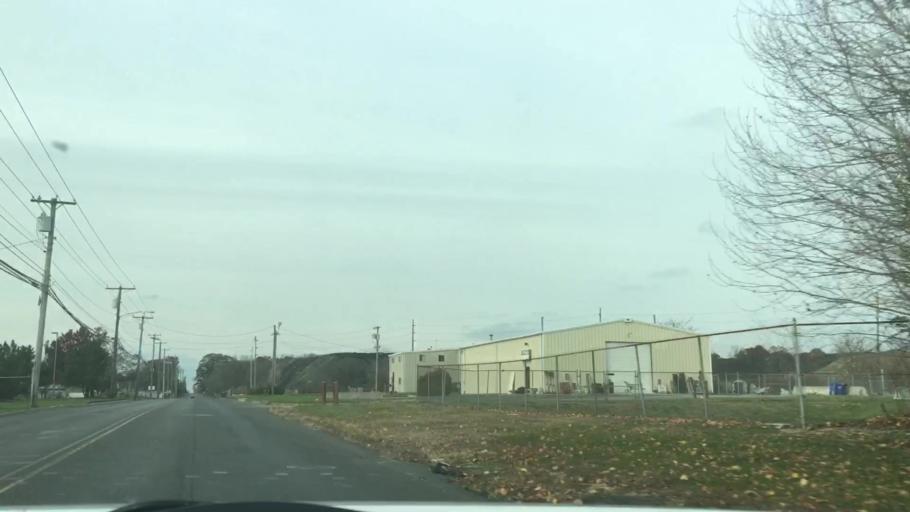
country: US
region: New Jersey
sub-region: Atlantic County
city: Pleasantville
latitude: 39.3991
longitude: -74.5369
